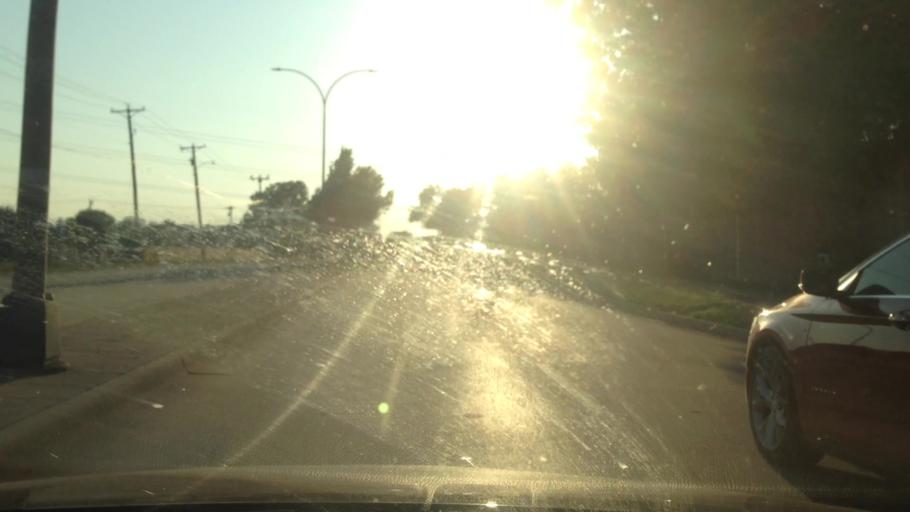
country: US
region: Texas
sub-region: Tarrant County
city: Dalworthington Gardens
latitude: 32.6449
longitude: -97.1189
